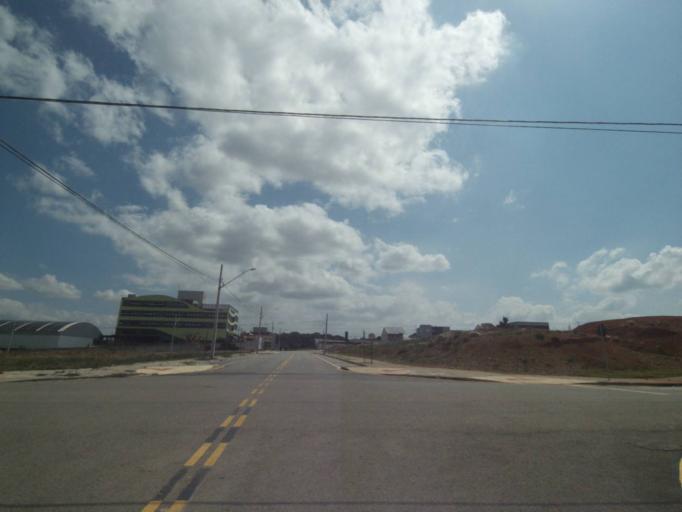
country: BR
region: Parana
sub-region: Curitiba
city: Curitiba
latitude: -25.5079
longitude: -49.3085
